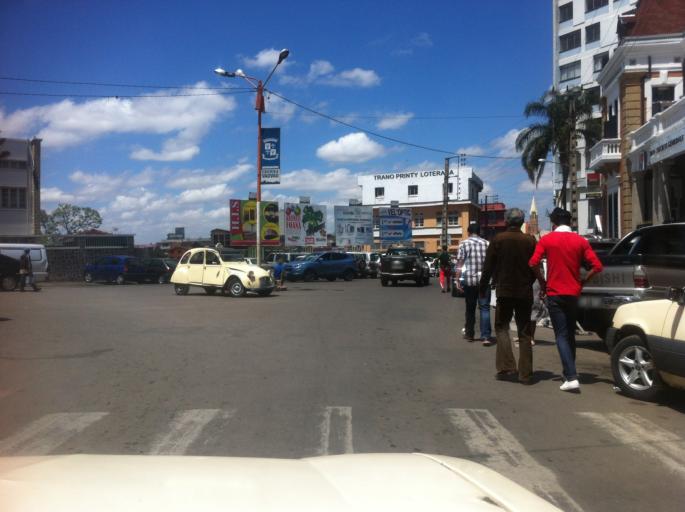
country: MG
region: Analamanga
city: Antananarivo
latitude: -18.9094
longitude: 47.5246
